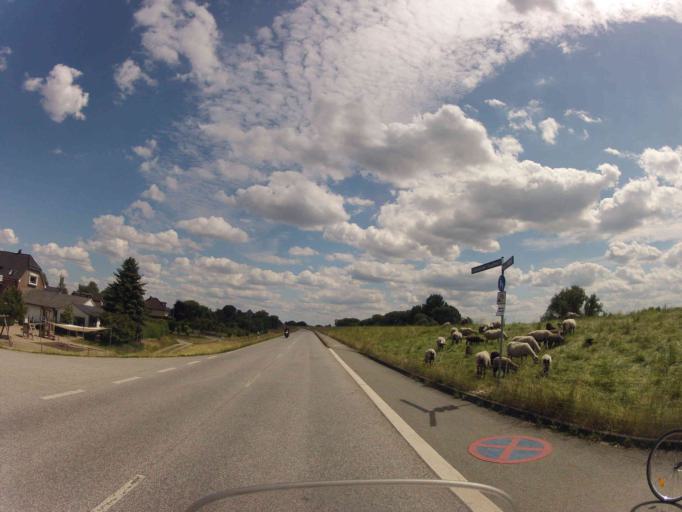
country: DE
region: Lower Saxony
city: Stelle
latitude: 53.4062
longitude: 10.1586
